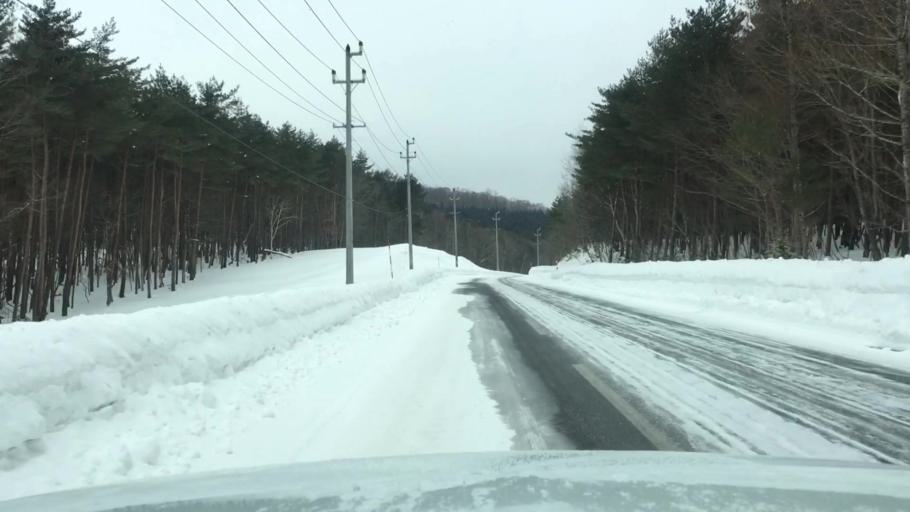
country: JP
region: Iwate
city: Shizukuishi
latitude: 39.9745
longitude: 141.0017
